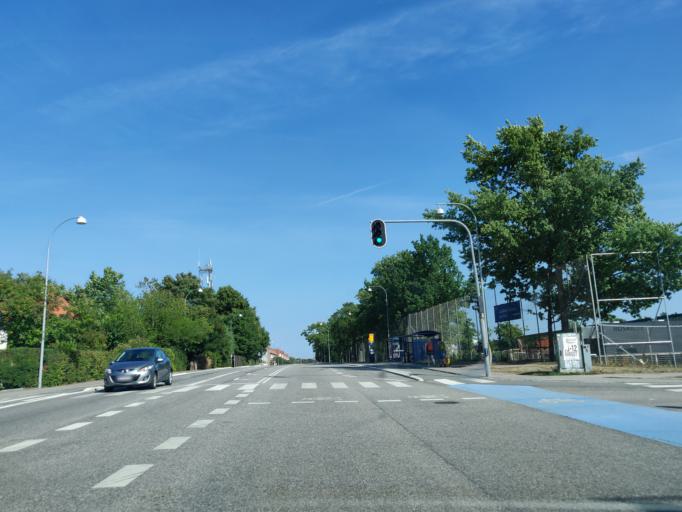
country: DK
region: Zealand
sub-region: Roskilde Kommune
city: Roskilde
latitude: 55.6356
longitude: 12.0568
